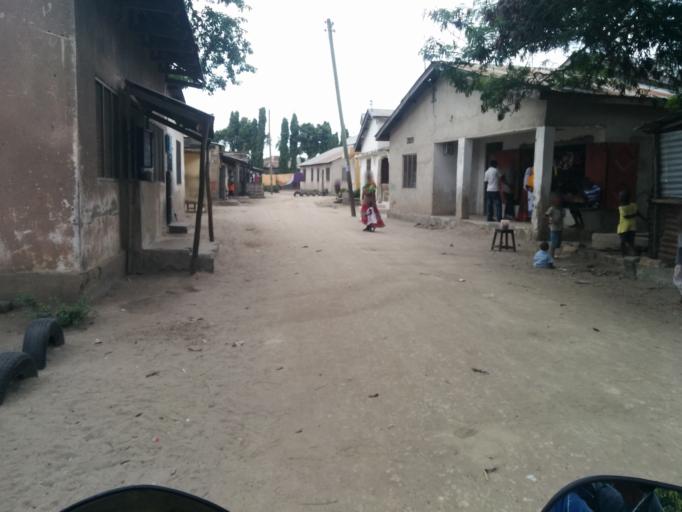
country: TZ
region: Dar es Salaam
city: Dar es Salaam
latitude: -6.8721
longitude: 39.2468
